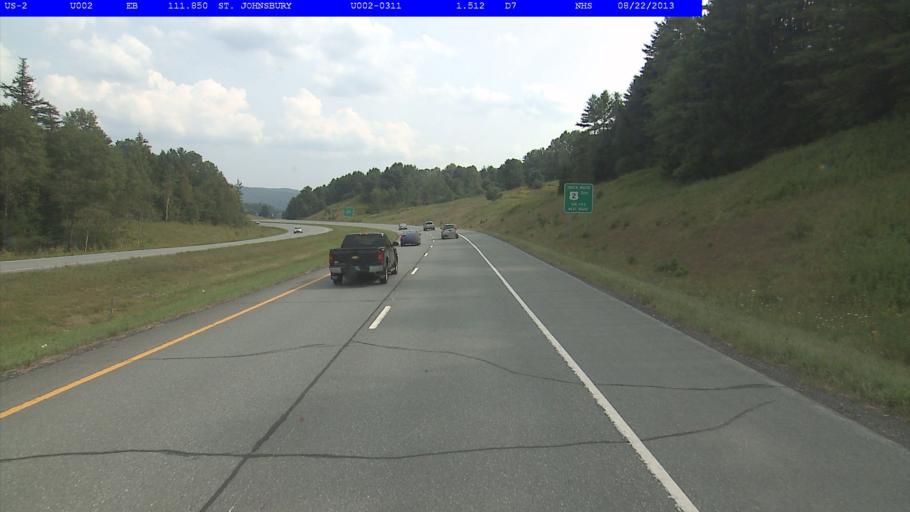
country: US
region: Vermont
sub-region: Caledonia County
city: St Johnsbury
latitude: 44.4330
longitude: -72.0407
